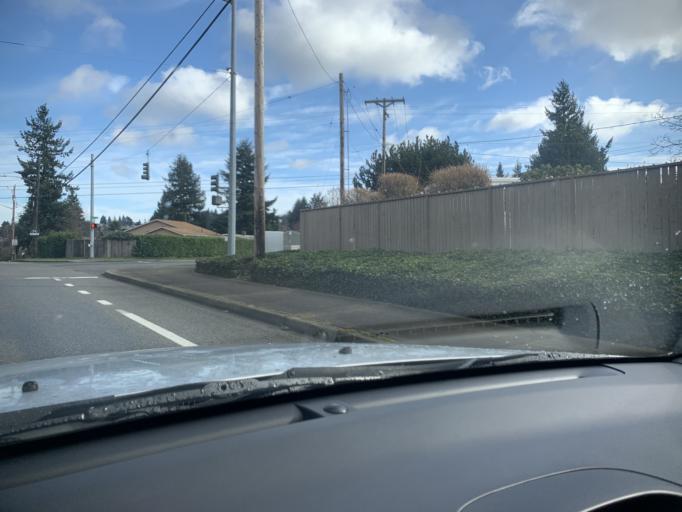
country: US
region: Washington
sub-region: Pierce County
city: University Place
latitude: 47.2653
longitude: -122.5363
